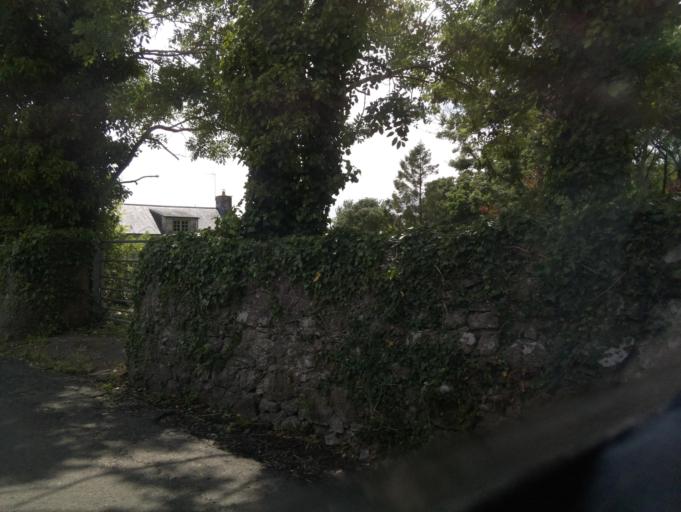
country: GB
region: Wales
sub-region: Vale of Glamorgan
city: Wick
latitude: 51.4065
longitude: -3.5313
